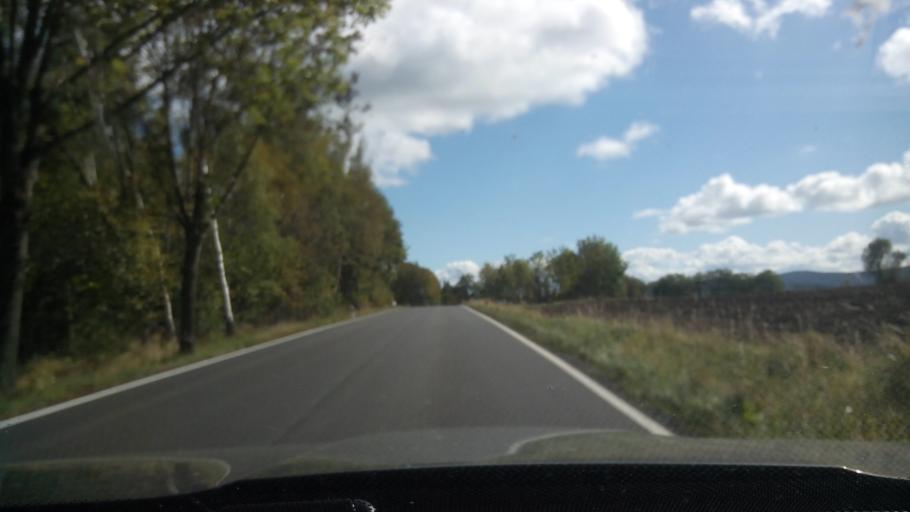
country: CZ
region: Jihocesky
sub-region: Okres Prachatice
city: Stachy
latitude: 49.1118
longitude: 13.6506
